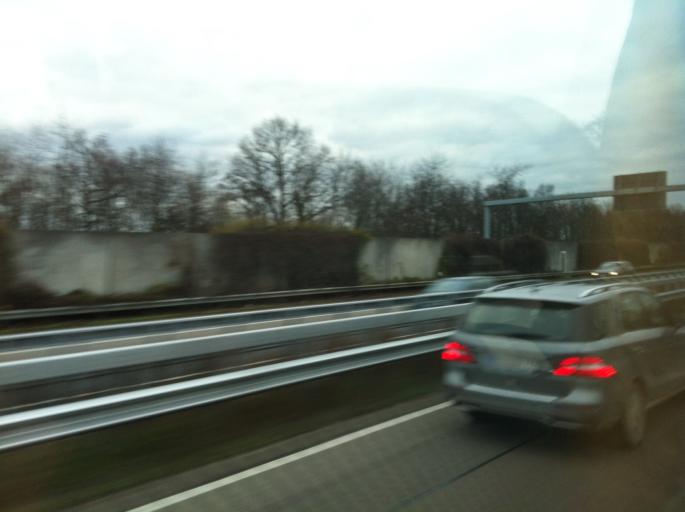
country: DE
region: Rheinland-Pfalz
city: Ockenheim
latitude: 49.9600
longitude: 7.9574
